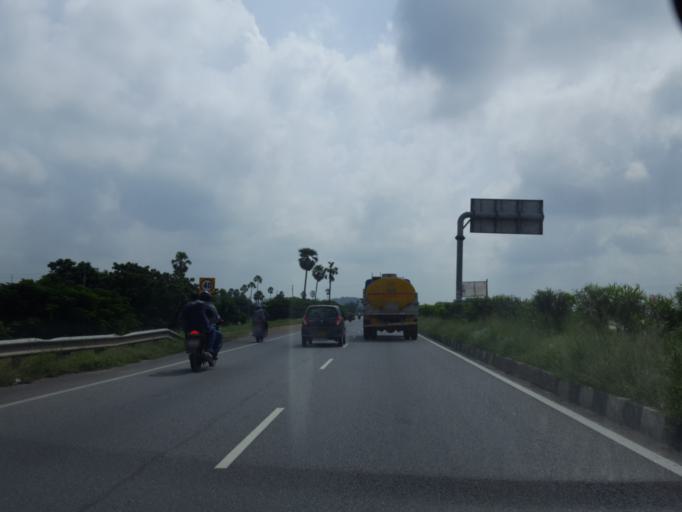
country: IN
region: Telangana
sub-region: Nalgonda
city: Bhongir
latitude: 17.2307
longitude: 78.9676
